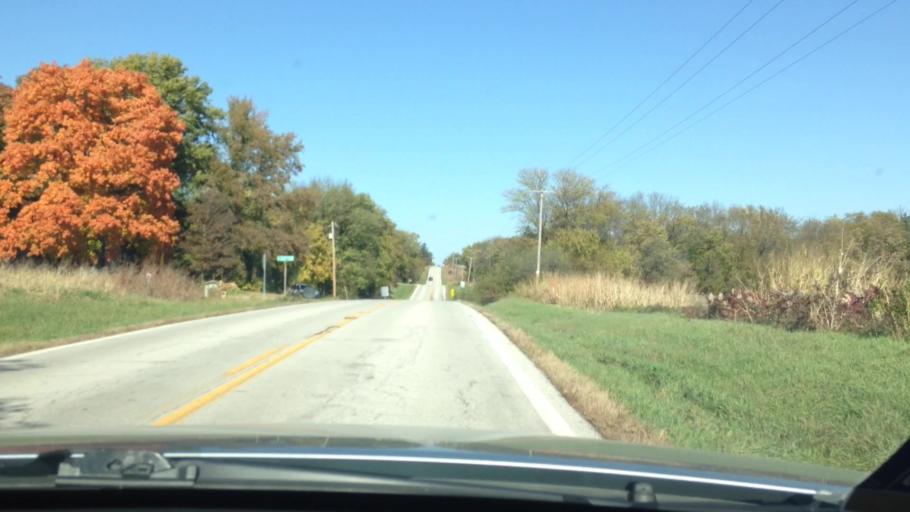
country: US
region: Missouri
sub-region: Platte County
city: Weatherby Lake
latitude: 39.3172
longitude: -94.6488
